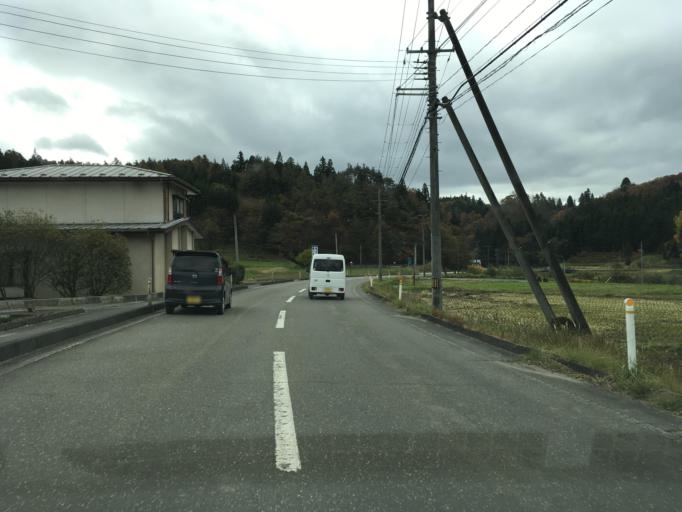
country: JP
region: Iwate
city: Mizusawa
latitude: 39.0609
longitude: 141.3618
